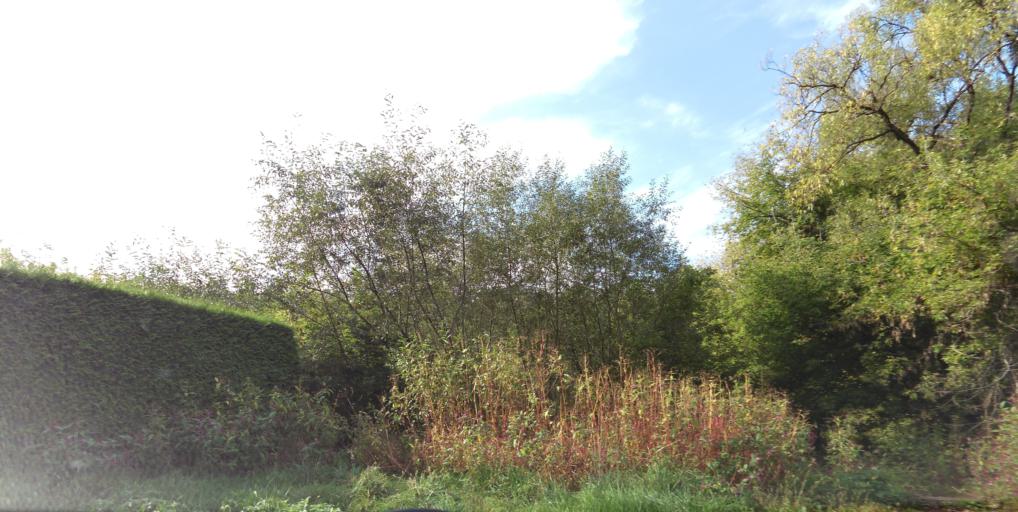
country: LT
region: Vilnius County
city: Vilkpede
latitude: 54.6894
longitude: 25.2453
